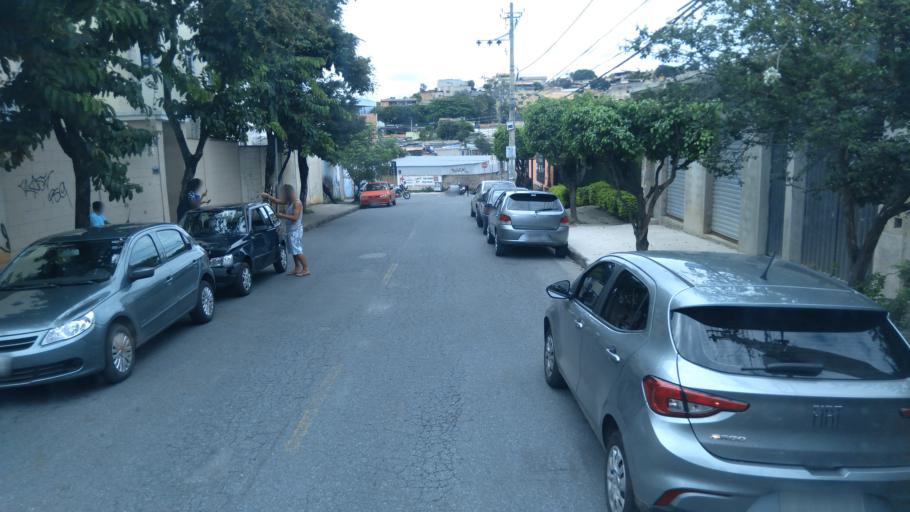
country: BR
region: Minas Gerais
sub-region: Belo Horizonte
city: Belo Horizonte
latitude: -19.8502
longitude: -43.9057
